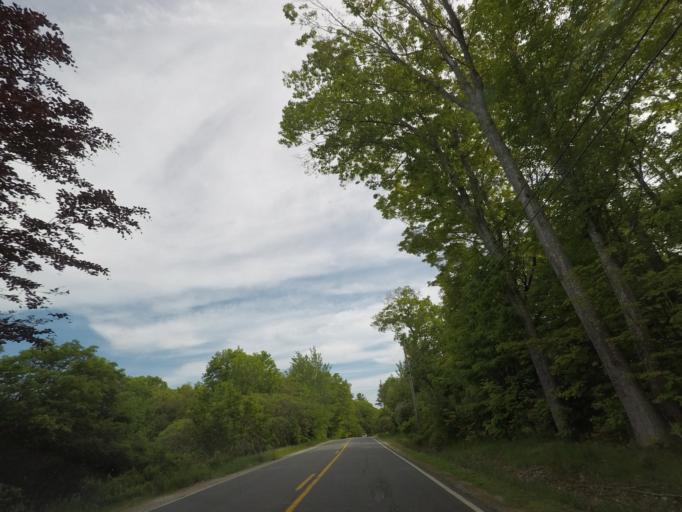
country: US
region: Maine
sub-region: Sagadahoc County
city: Richmond
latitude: 44.1233
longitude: -69.7759
